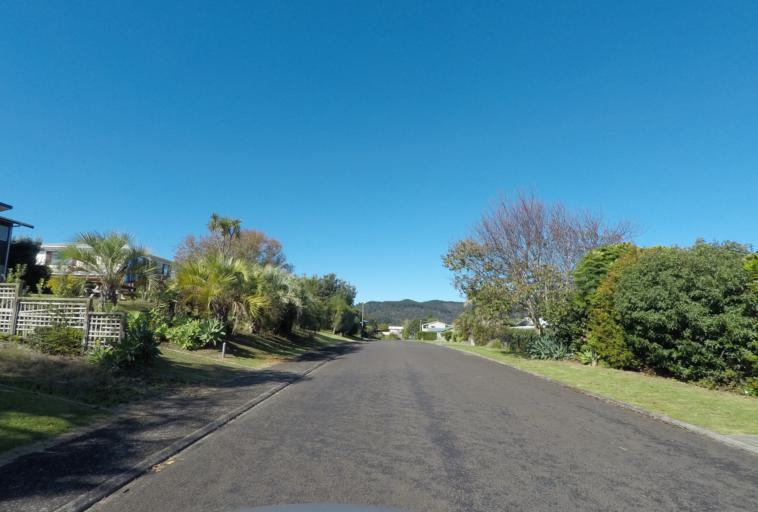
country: NZ
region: Waikato
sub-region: Thames-Coromandel District
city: Whangamata
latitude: -37.2814
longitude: 175.9001
